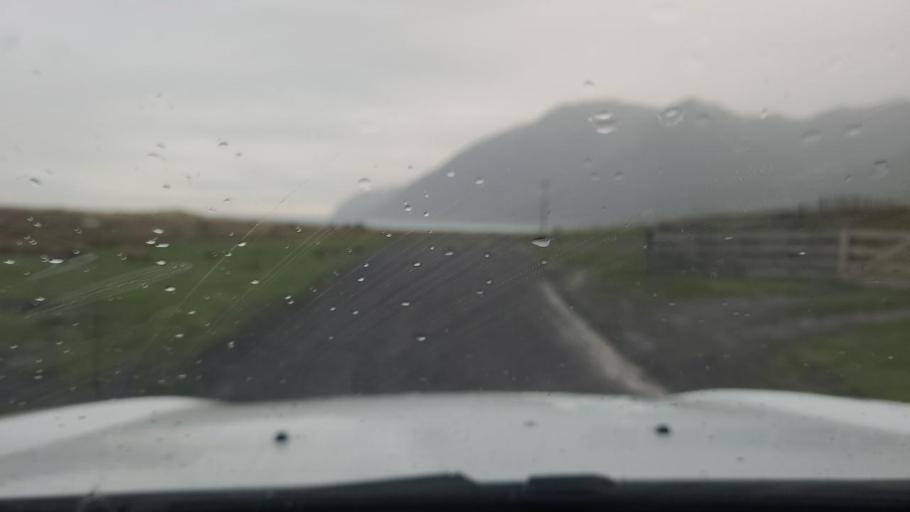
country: NZ
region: Wellington
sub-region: South Wairarapa District
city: Waipawa
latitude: -41.5670
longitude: 175.3952
